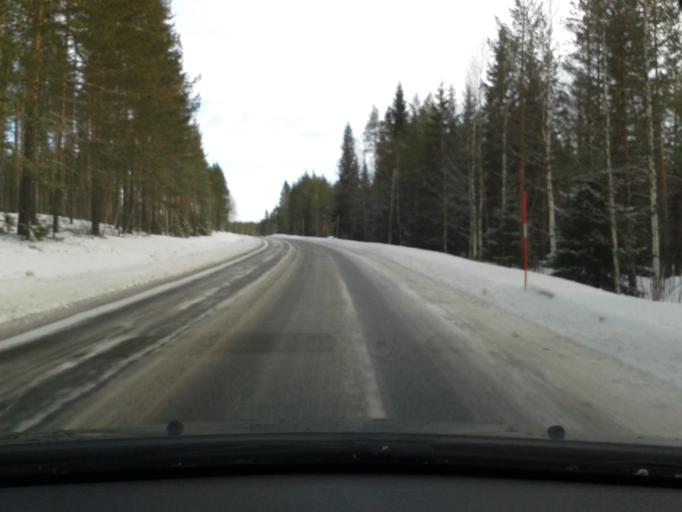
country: SE
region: Vaesterbotten
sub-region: Vilhelmina Kommun
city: Vilhelmina
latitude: 64.6470
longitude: 16.5287
